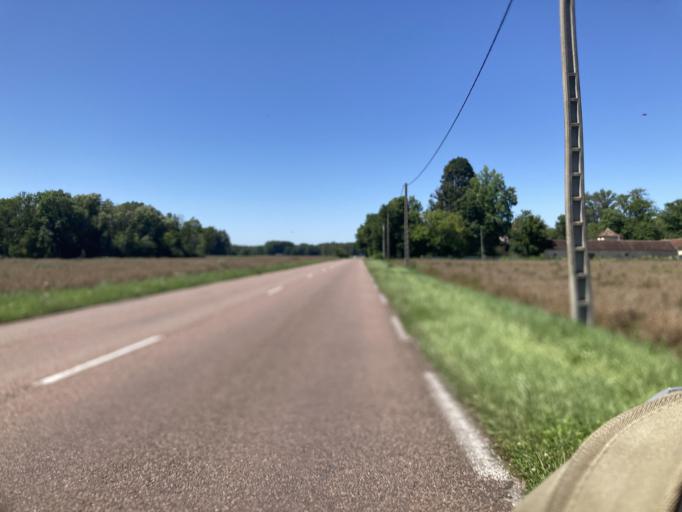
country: FR
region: Bourgogne
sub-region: Departement de l'Yonne
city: Laroche-Saint-Cydroine
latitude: 47.9641
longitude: 3.4797
